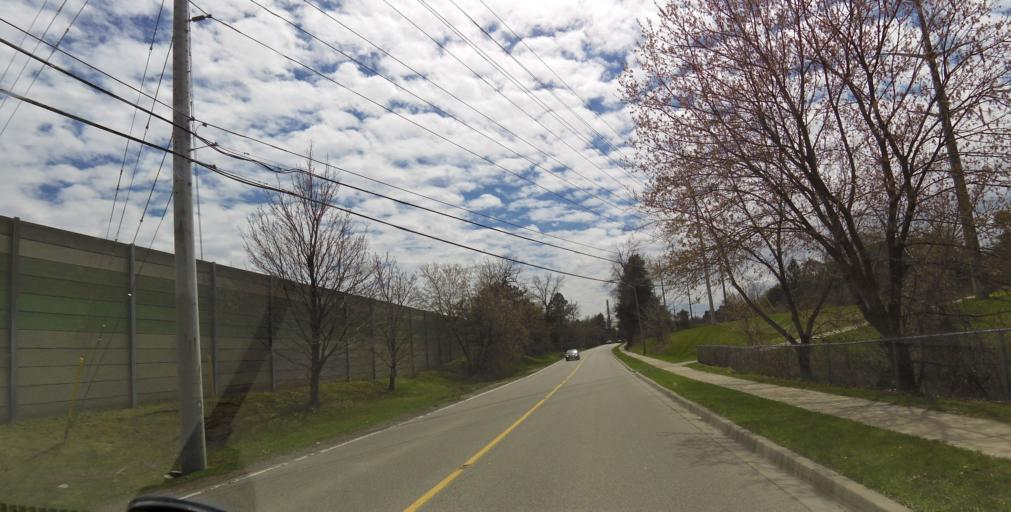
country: CA
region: Ontario
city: Mississauga
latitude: 43.5625
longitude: -79.6061
